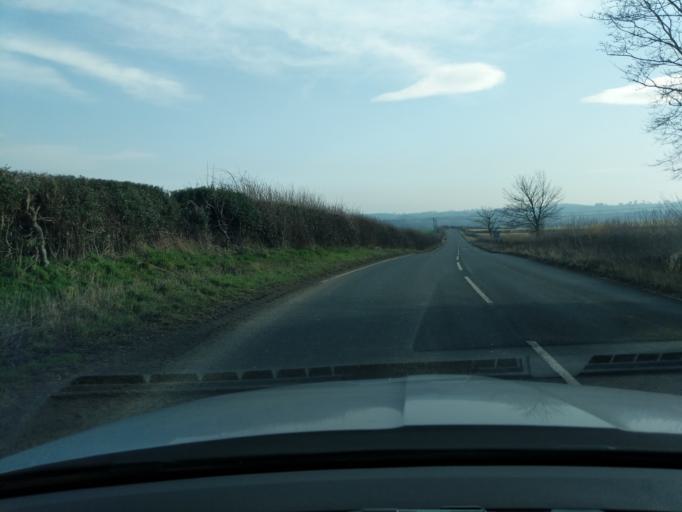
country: GB
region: England
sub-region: North Yorkshire
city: Catterick
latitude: 54.3179
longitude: -1.6760
